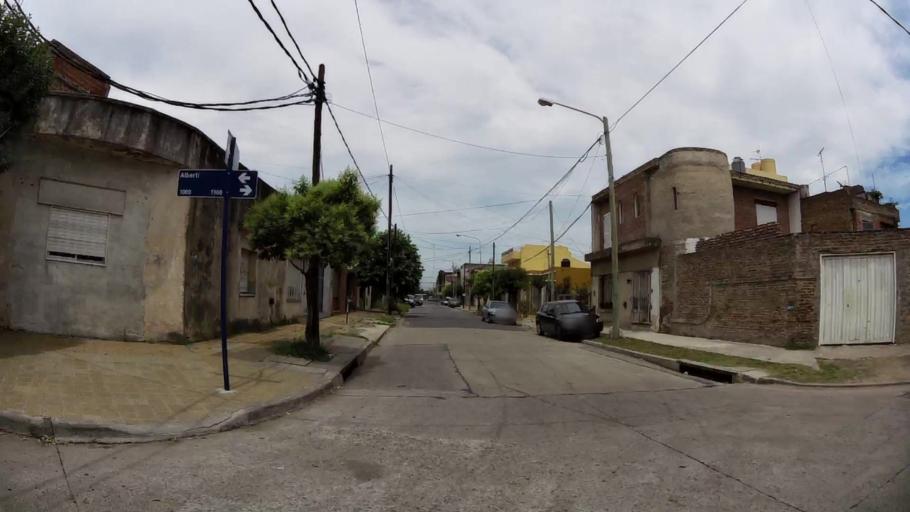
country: AR
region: Buenos Aires
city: San Justo
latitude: -34.6855
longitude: -58.5311
